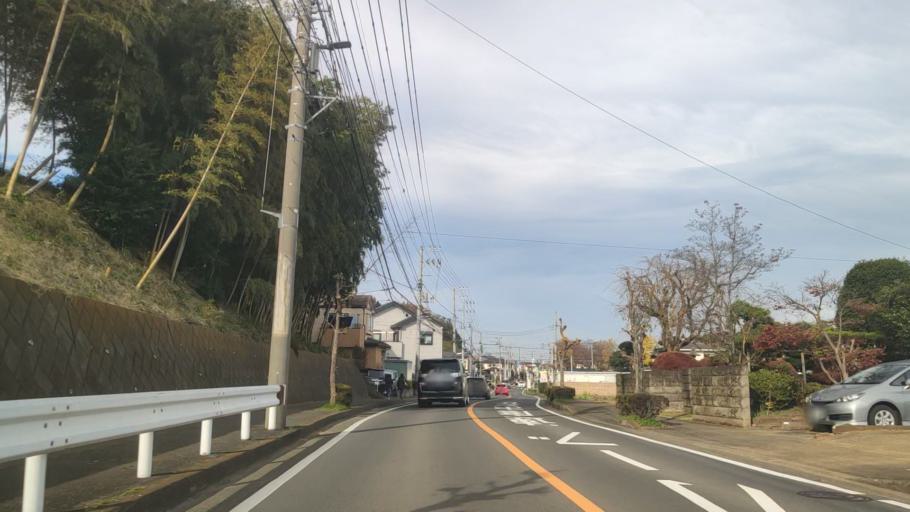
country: JP
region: Kanagawa
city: Atsugi
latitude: 35.4311
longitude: 139.4045
